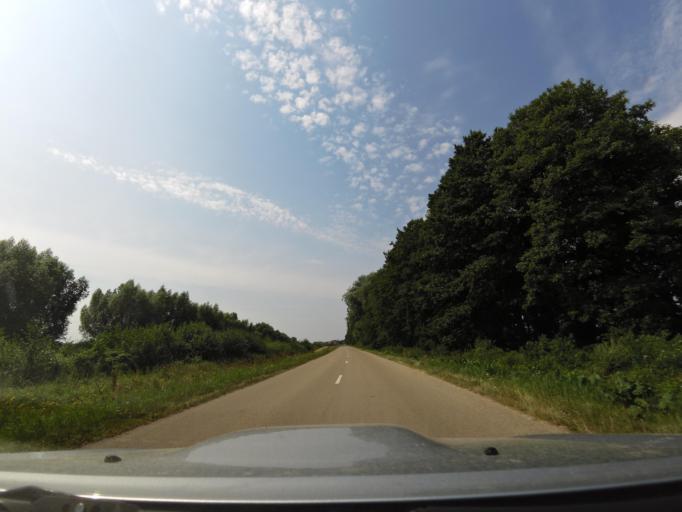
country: LT
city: Rusne
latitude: 55.3455
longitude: 21.3037
